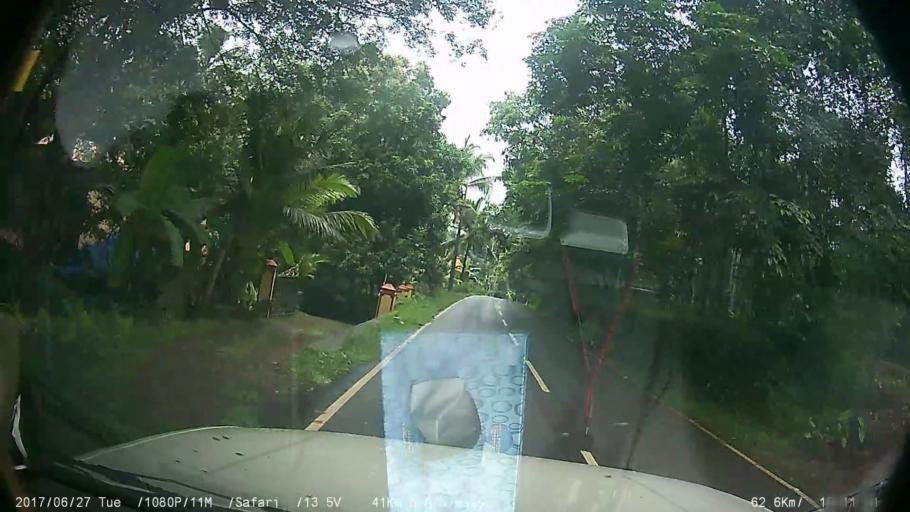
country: IN
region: Kerala
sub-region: Kottayam
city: Palackattumala
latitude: 9.7737
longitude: 76.5483
